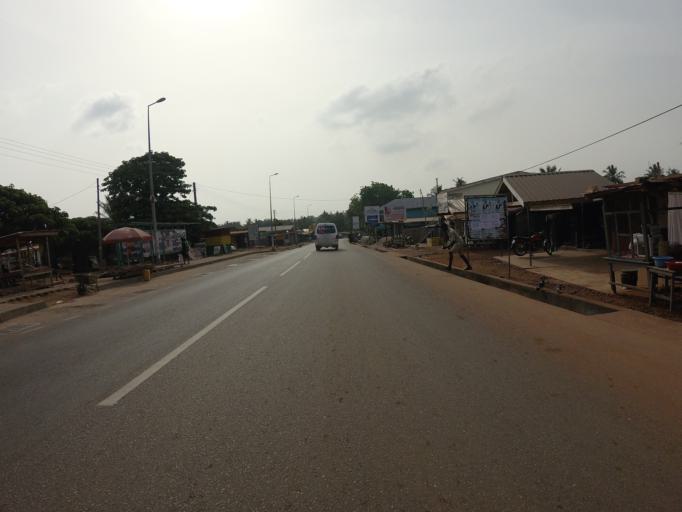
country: GH
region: Volta
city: Ho
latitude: 6.6146
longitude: 0.4744
